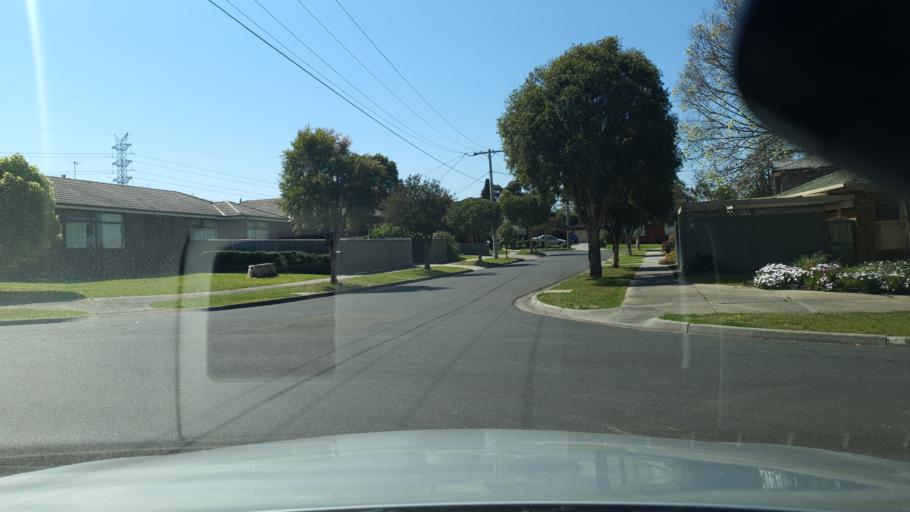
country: AU
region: Victoria
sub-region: Greater Dandenong
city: Noble Park North
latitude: -37.9299
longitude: 145.1777
